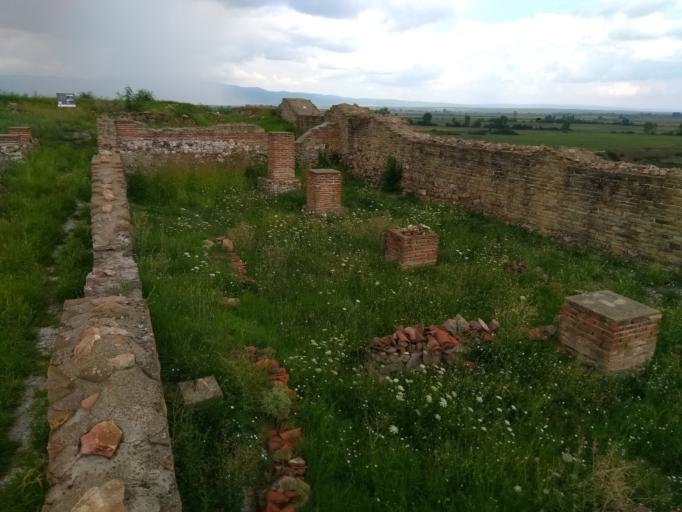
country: BG
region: Yambol
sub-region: Obshtina Yambol
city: Yambol
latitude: 42.5511
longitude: 26.4860
